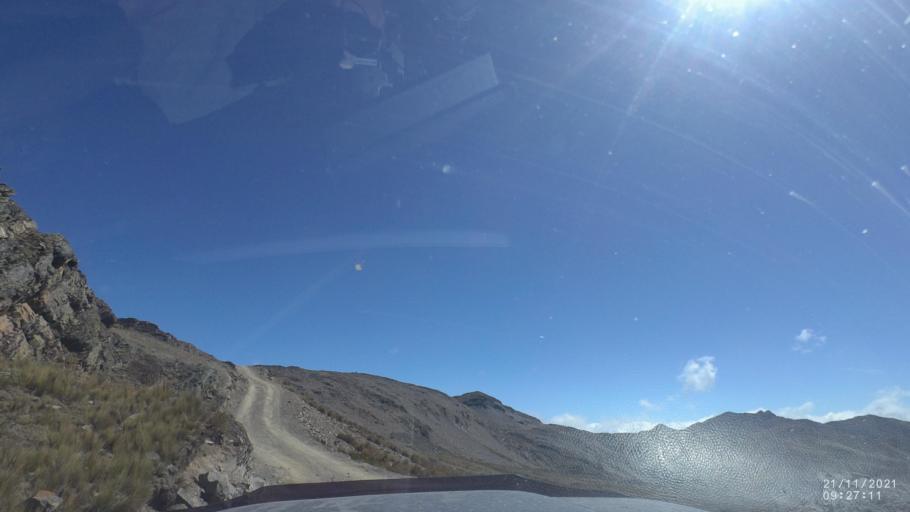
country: BO
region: Cochabamba
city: Cochabamba
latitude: -17.0848
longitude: -66.2510
